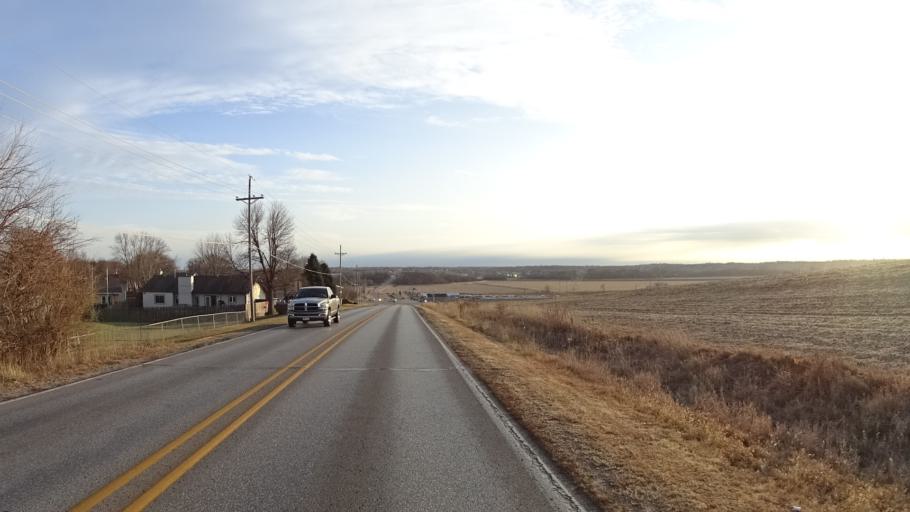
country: US
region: Nebraska
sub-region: Sarpy County
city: Offutt Air Force Base
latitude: 41.1650
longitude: -95.9672
